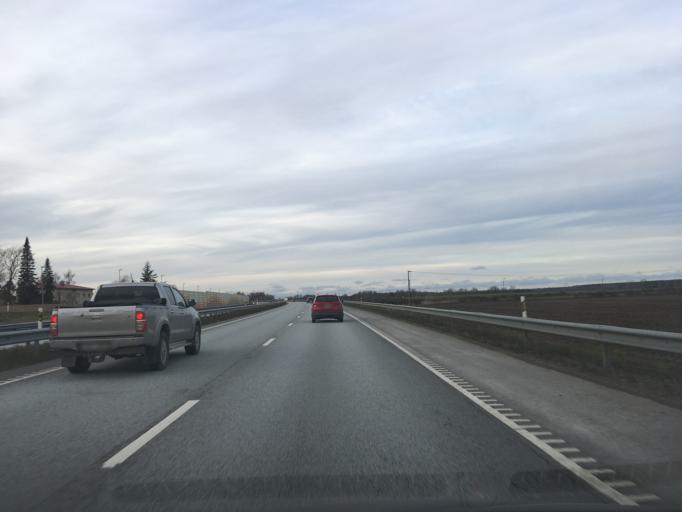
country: EE
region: Ida-Virumaa
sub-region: Johvi vald
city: Johvi
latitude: 59.3765
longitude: 27.3775
